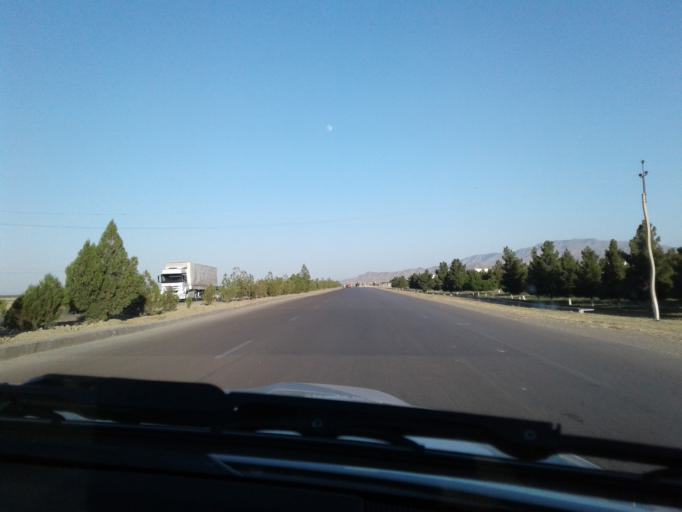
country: TM
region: Ahal
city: Baharly
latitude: 38.3212
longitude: 57.5951
